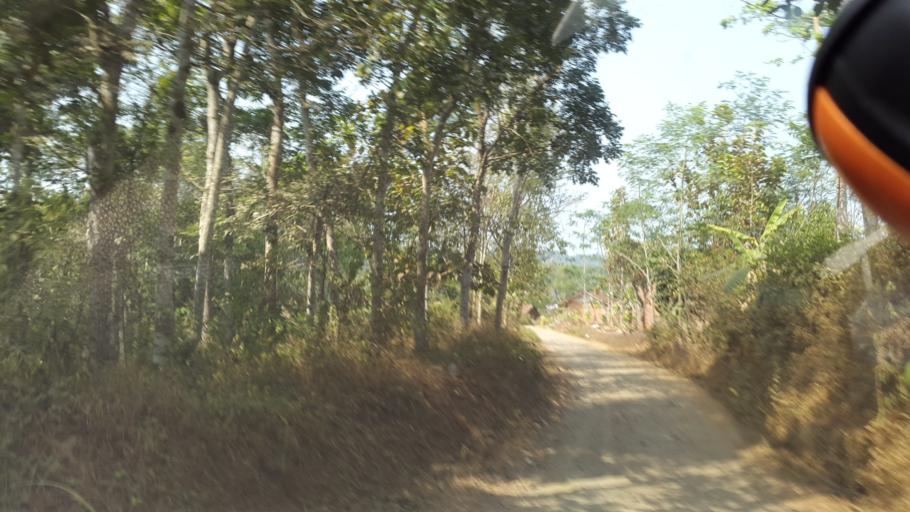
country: ID
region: West Java
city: Citampian
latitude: -7.1639
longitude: 106.7603
